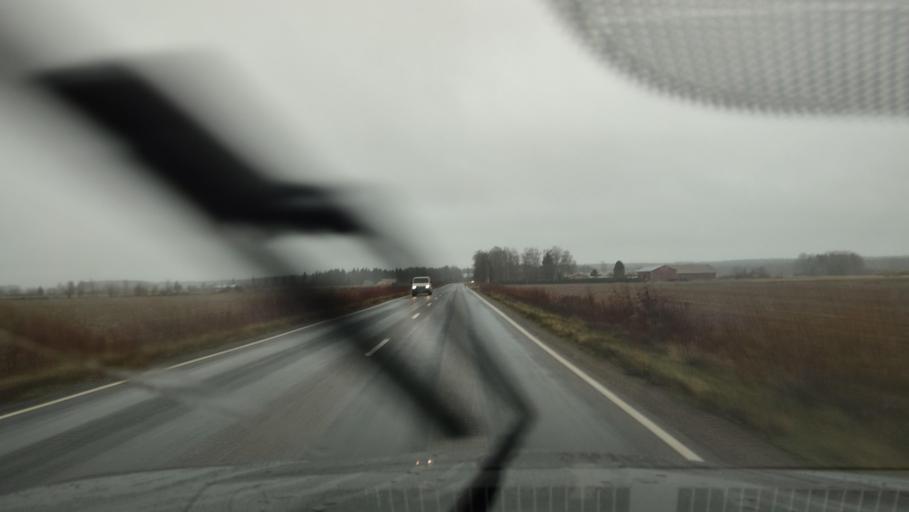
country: FI
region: Southern Ostrobothnia
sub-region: Suupohja
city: Karijoki
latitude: 62.2352
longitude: 21.6664
